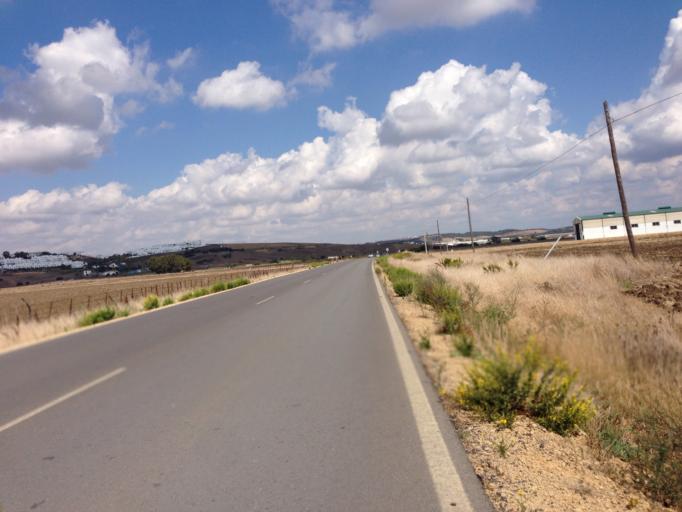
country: ES
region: Andalusia
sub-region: Provincia de Cadiz
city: Conil de la Frontera
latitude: 36.2670
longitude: -6.0741
